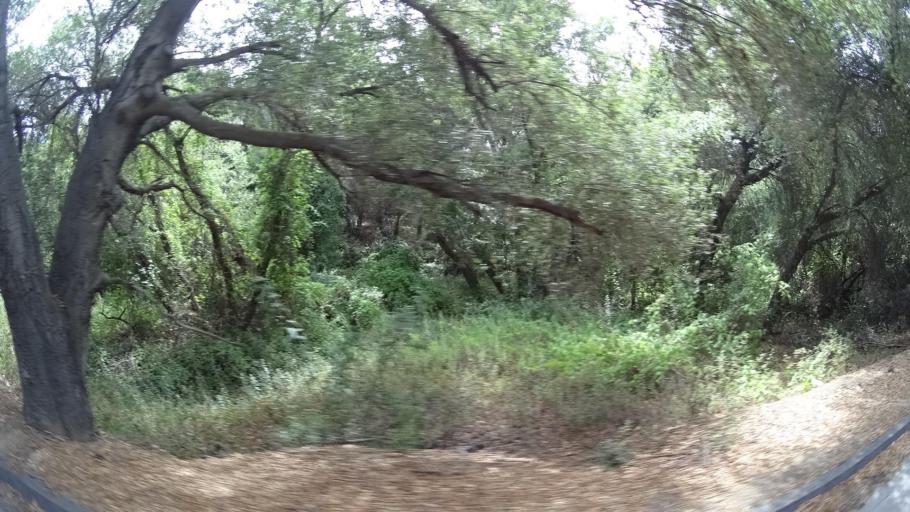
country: US
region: California
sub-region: San Diego County
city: Fallbrook
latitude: 33.4152
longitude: -117.2373
